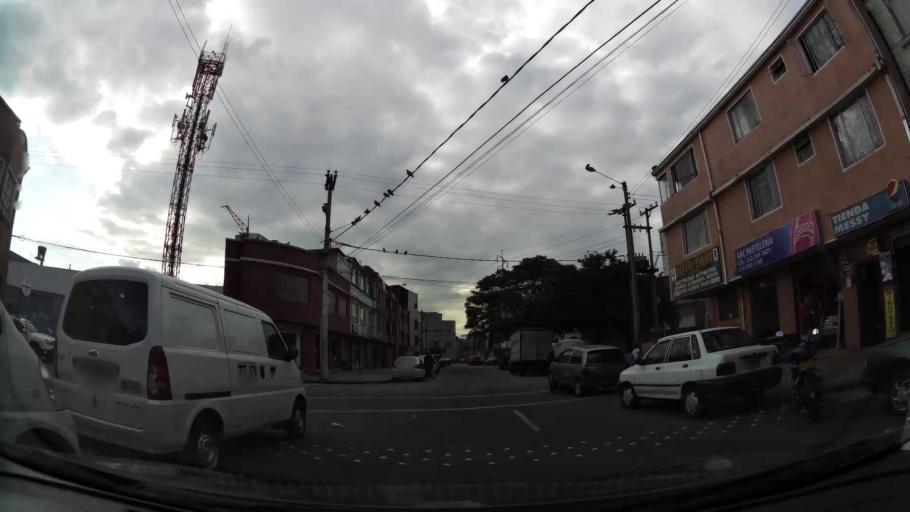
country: CO
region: Bogota D.C.
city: Bogota
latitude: 4.6548
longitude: -74.0696
